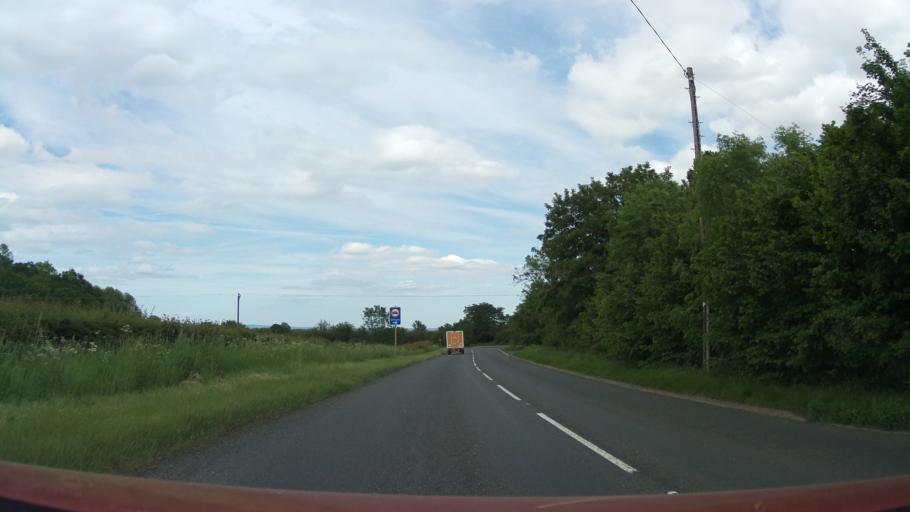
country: GB
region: England
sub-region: Worcestershire
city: Great Malvern
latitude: 52.1445
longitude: -2.3469
